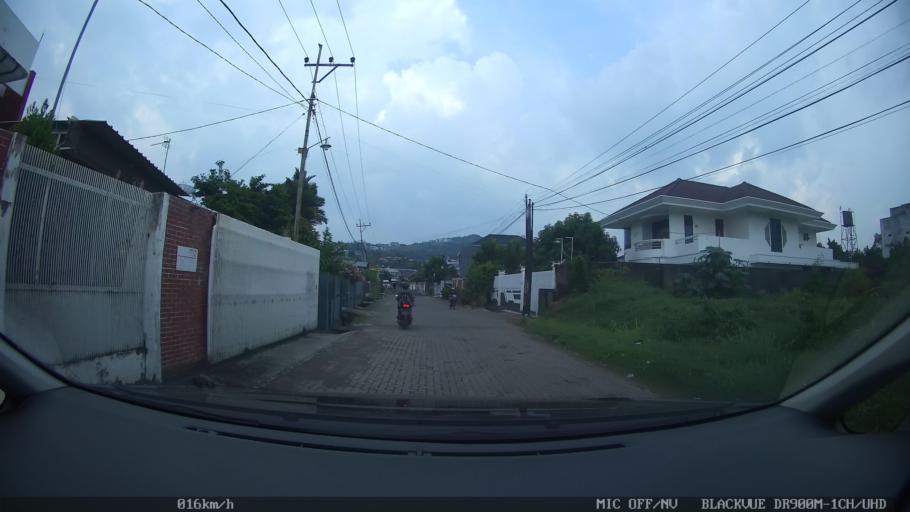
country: ID
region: Lampung
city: Bandarlampung
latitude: -5.4410
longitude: 105.2800
